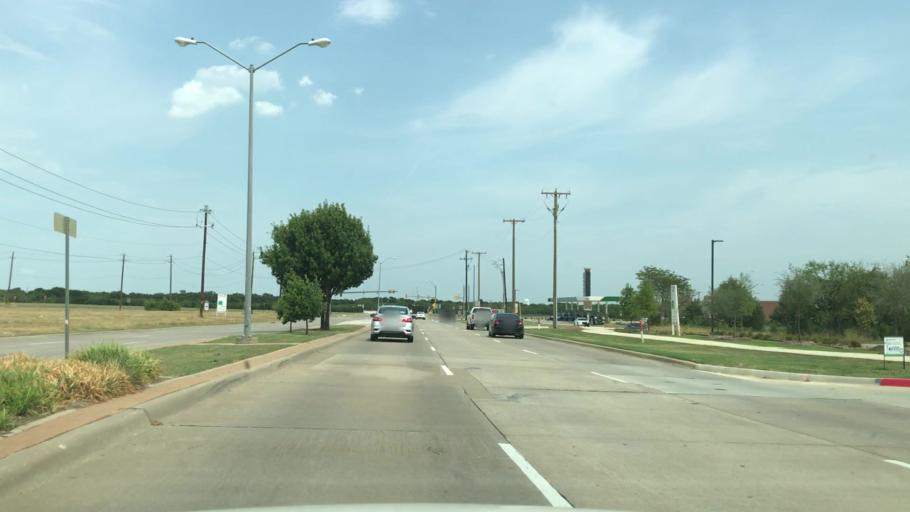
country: US
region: Texas
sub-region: Tarrant County
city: Euless
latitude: 32.8516
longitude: -97.0680
